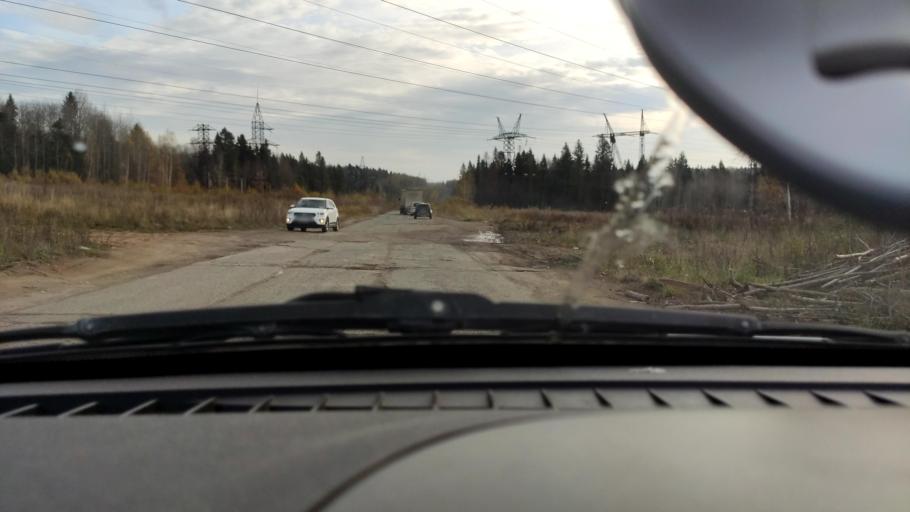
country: RU
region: Perm
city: Perm
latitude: 58.0886
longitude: 56.4194
